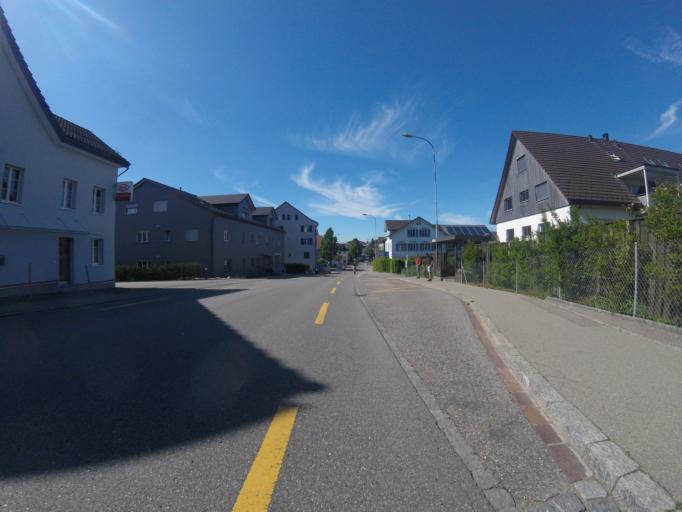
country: CH
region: Saint Gallen
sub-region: Wahlkreis Wil
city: Wil
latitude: 47.4475
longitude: 9.0502
